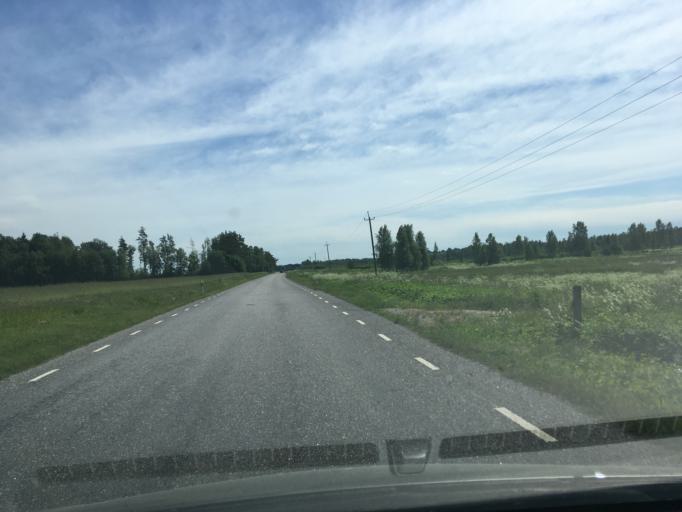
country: EE
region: Paernumaa
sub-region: Audru vald
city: Audru
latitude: 58.4292
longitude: 24.4090
